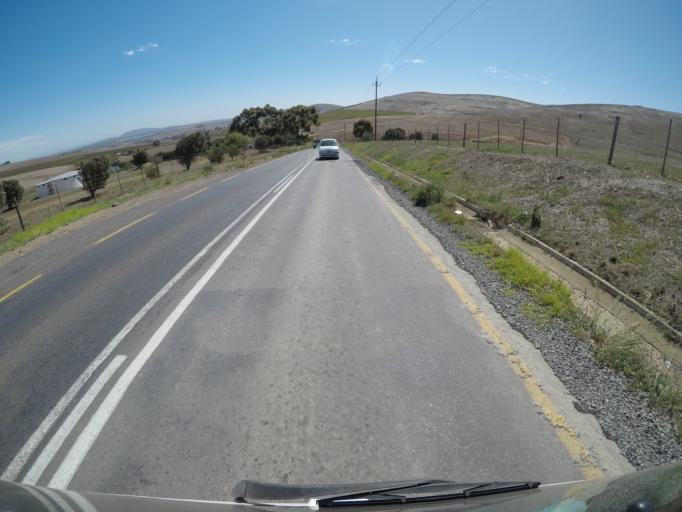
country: ZA
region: Western Cape
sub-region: City of Cape Town
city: Kraaifontein
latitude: -33.7945
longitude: 18.6053
